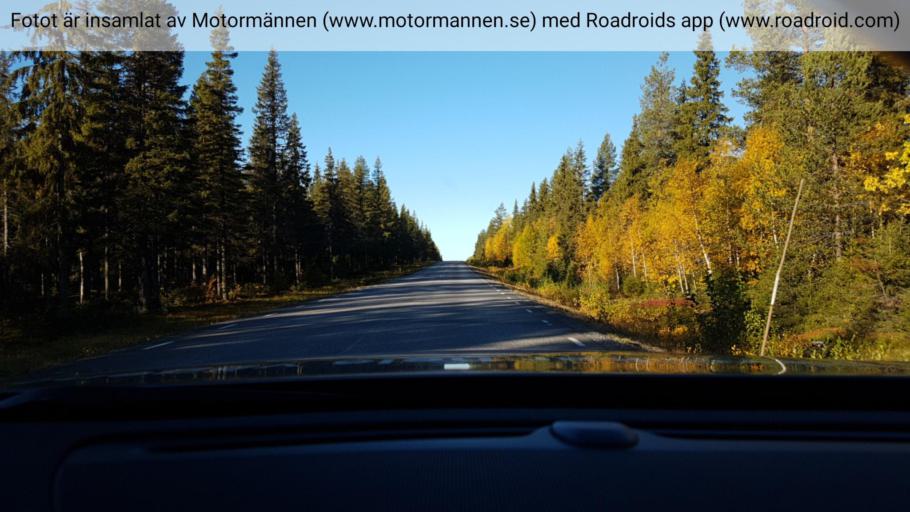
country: SE
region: Vaesterbotten
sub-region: Skelleftea Kommun
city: Storvik
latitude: 65.3268
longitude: 20.7473
